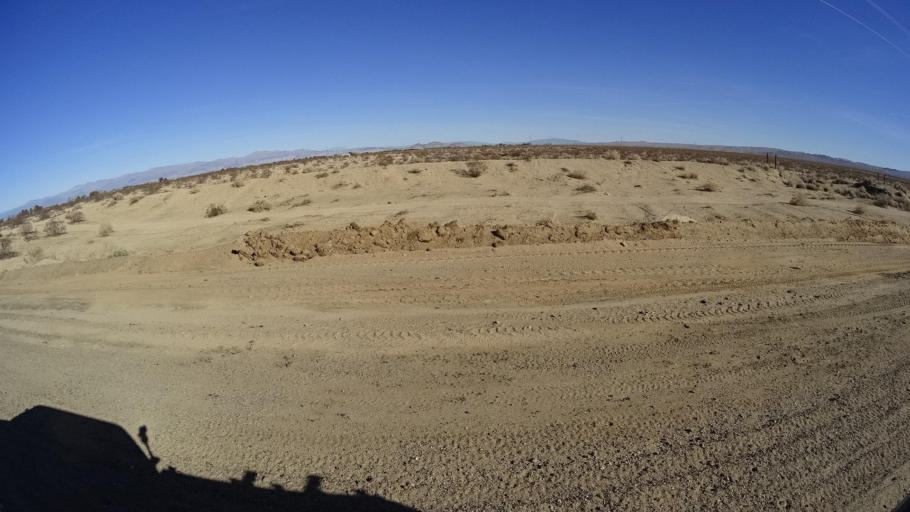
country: US
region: California
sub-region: Kern County
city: Inyokern
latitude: 35.6202
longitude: -117.8044
